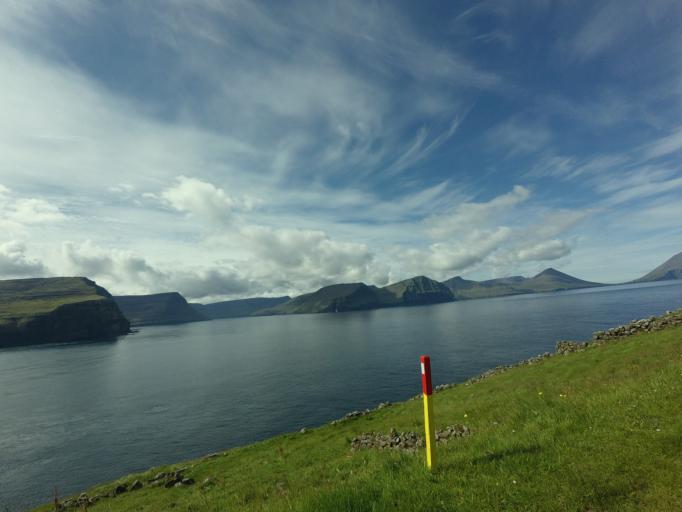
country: FO
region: Nordoyar
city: Klaksvik
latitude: 62.3211
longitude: -6.3243
